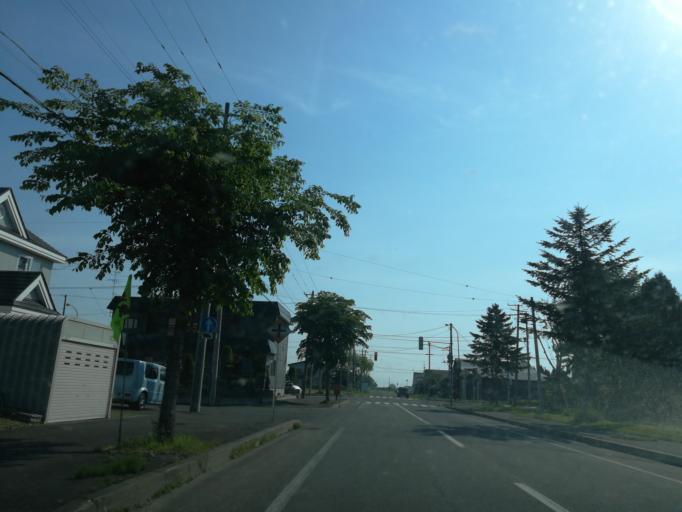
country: JP
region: Hokkaido
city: Iwamizawa
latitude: 43.1732
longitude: 141.7107
